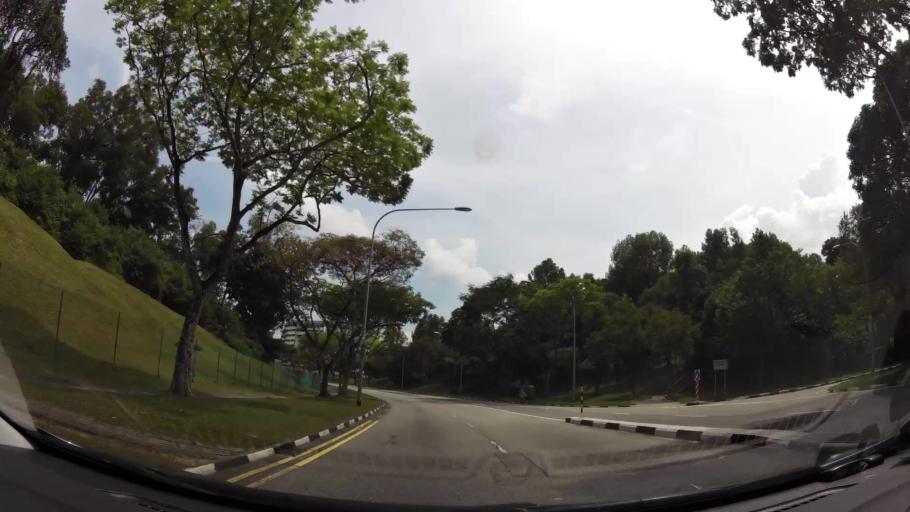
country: SG
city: Singapore
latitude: 1.3479
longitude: 103.7504
